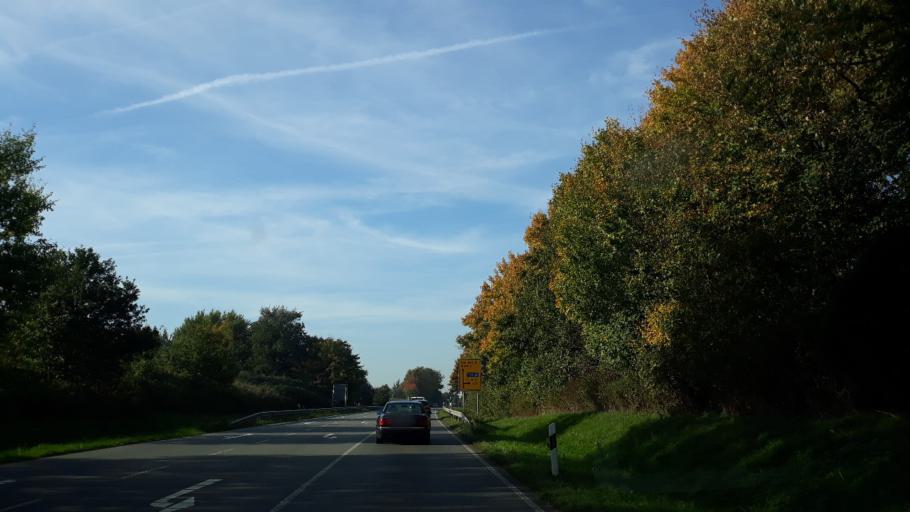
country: DE
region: Schleswig-Holstein
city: Schleswig
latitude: 54.5352
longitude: 9.5584
